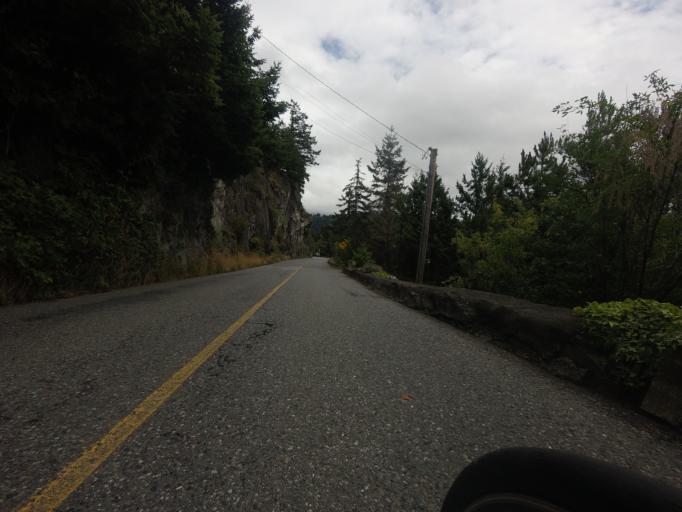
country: CA
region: British Columbia
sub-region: Greater Vancouver Regional District
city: Bowen Island
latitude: 49.3558
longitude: -123.2776
